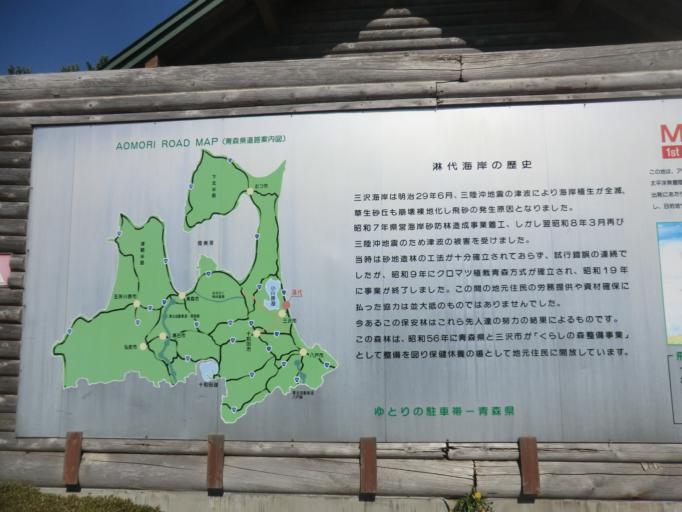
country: JP
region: Aomori
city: Misawa
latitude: 40.7422
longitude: 141.4101
